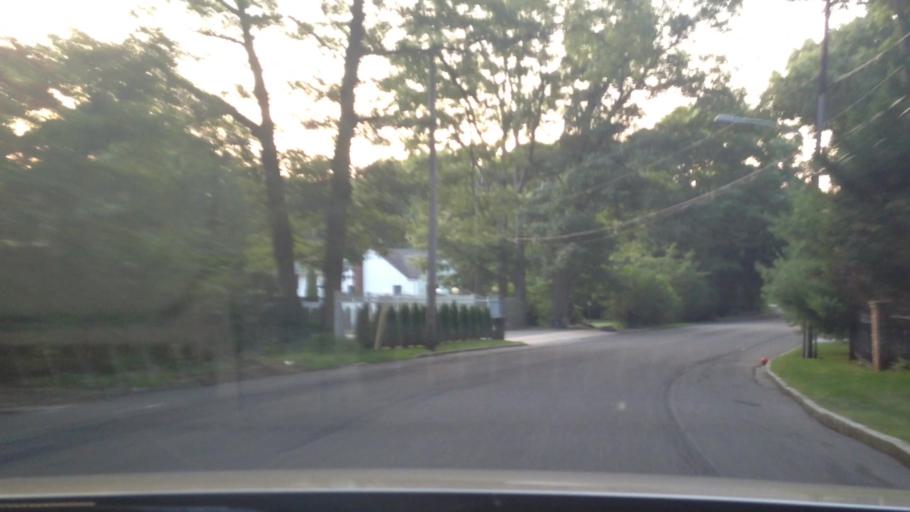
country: US
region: New York
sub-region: Suffolk County
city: South Huntington
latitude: 40.8093
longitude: -73.3825
